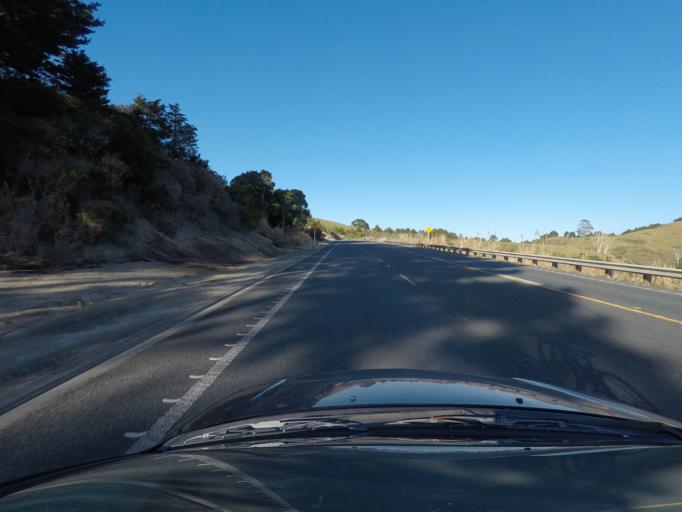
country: NZ
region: Northland
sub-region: Far North District
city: Kawakawa
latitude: -35.4821
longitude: 174.1241
